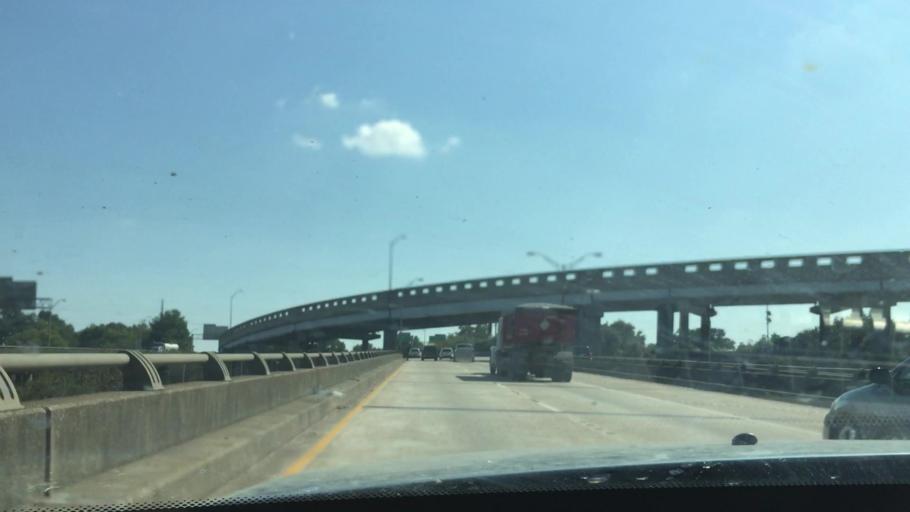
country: US
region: Louisiana
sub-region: East Baton Rouge Parish
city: Baton Rouge
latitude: 30.4398
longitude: -91.1784
